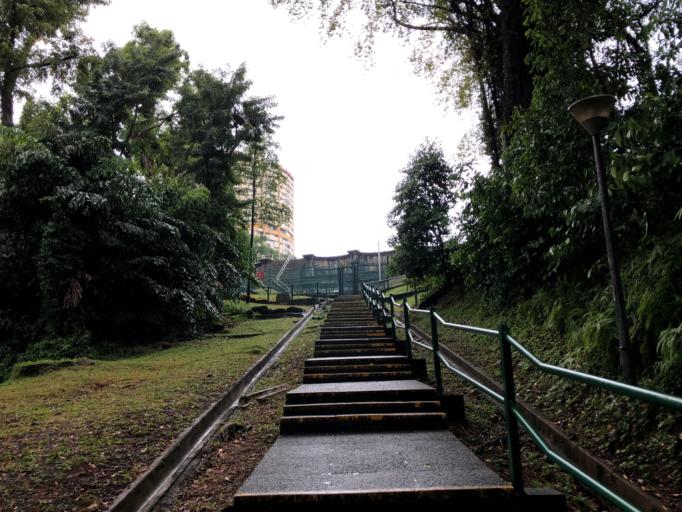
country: SG
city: Singapore
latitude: 1.2853
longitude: 103.8403
